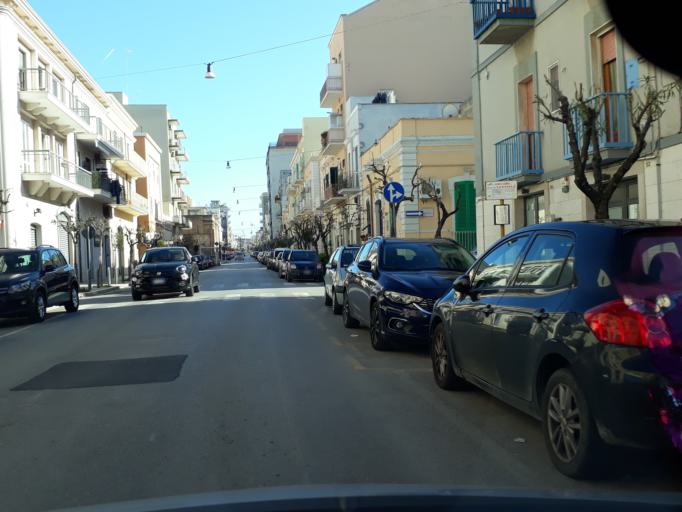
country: IT
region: Apulia
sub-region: Provincia di Bari
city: Monopoli
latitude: 40.9549
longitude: 17.2974
